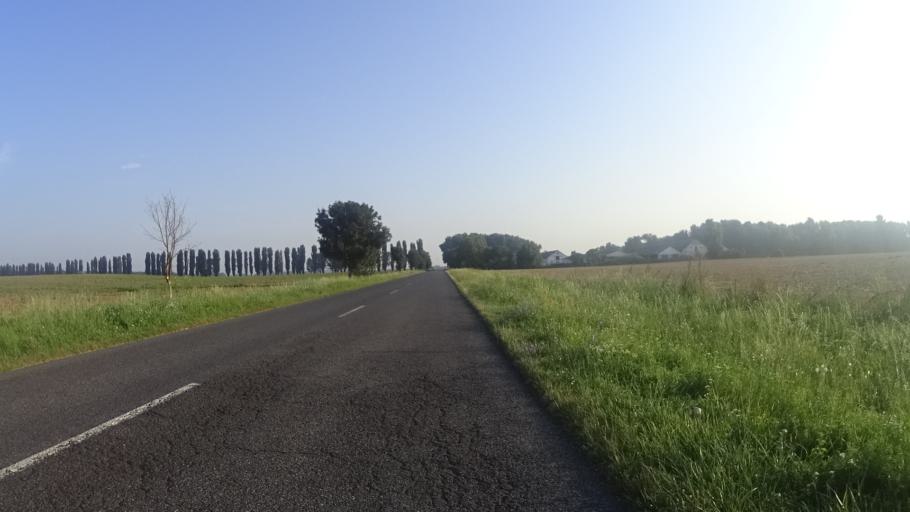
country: HU
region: Zala
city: Zalakomar
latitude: 46.6113
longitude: 17.1786
